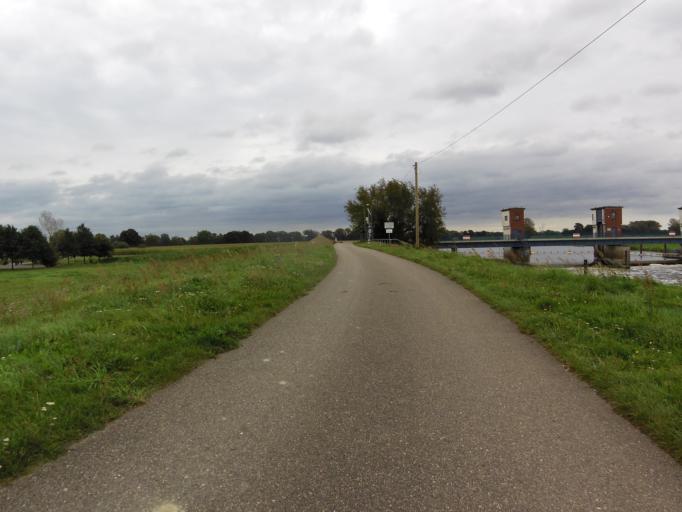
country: DE
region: Brandenburg
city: Ruhstadt
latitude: 52.9083
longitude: 11.8847
